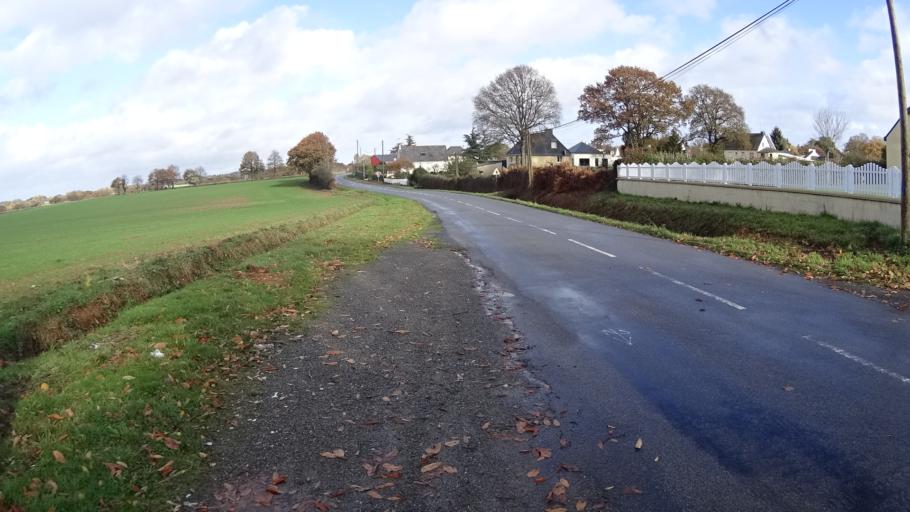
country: FR
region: Pays de la Loire
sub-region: Departement de la Loire-Atlantique
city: Saint-Nicolas-de-Redon
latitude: 47.6202
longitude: -2.0672
